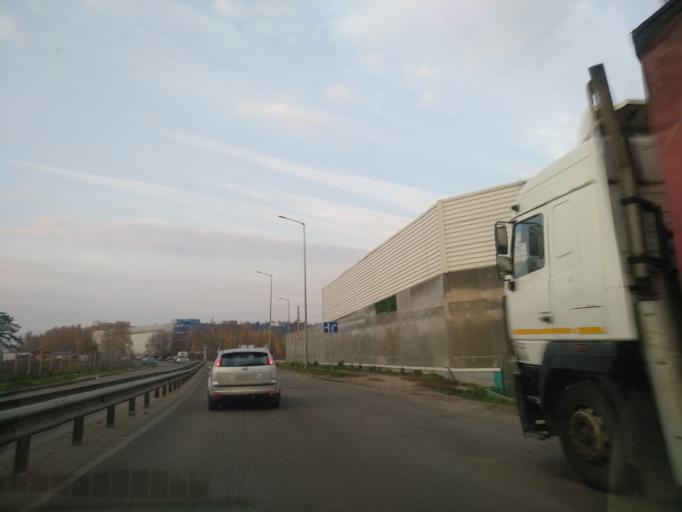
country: RU
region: Moscow
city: Lianozovo
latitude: 55.9154
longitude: 37.5715
